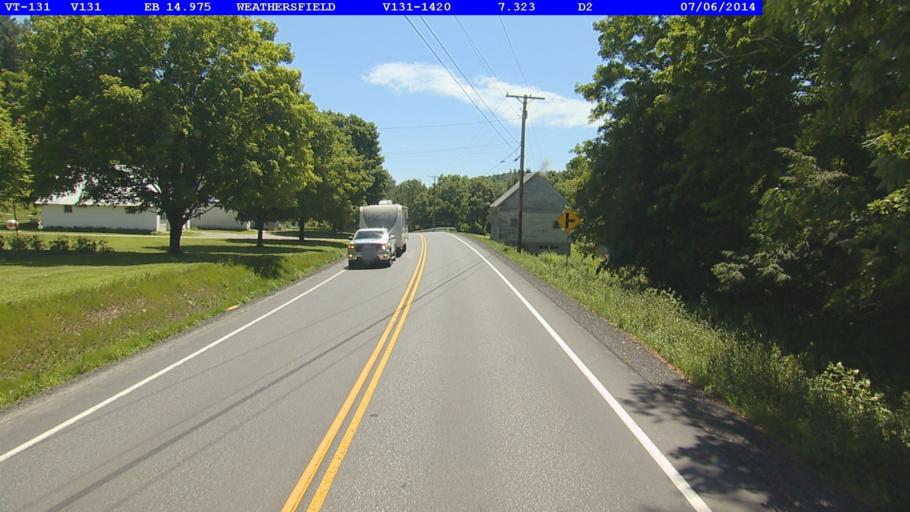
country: US
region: New Hampshire
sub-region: Sullivan County
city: Claremont
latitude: 43.4039
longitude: -72.4303
